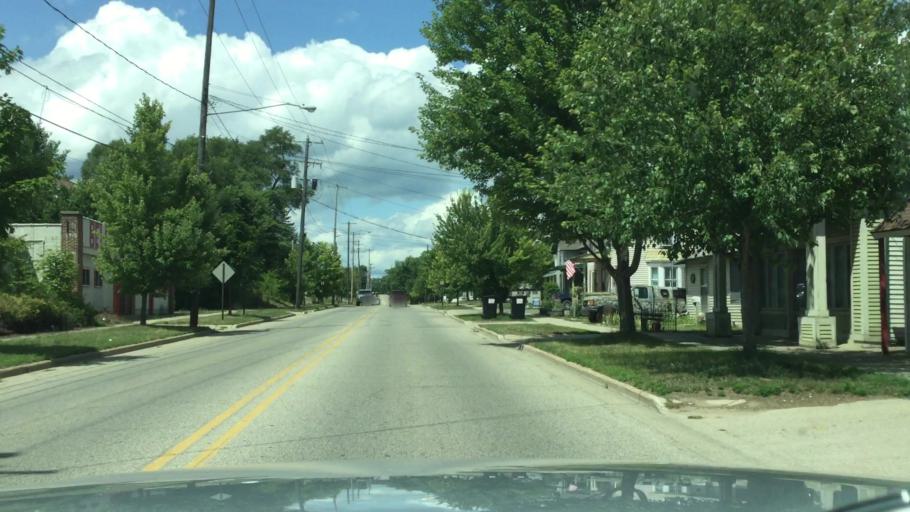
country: US
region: Michigan
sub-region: Ionia County
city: Belding
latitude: 43.1012
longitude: -85.2278
